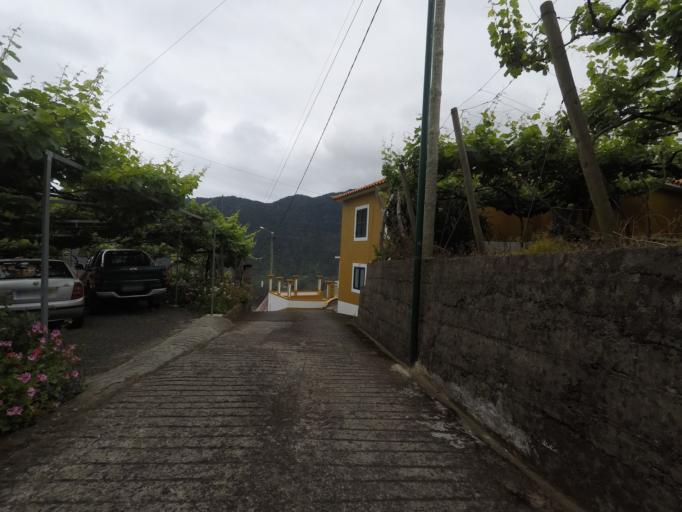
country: PT
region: Madeira
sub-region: Sao Vicente
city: Sao Vicente
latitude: 32.7862
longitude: -17.0422
